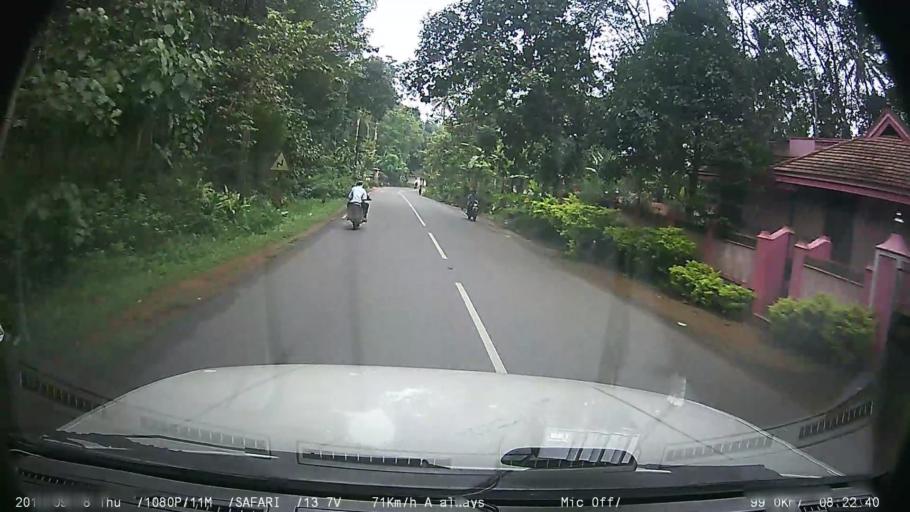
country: IN
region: Kerala
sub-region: Kottayam
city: Palackattumala
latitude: 9.6639
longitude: 76.6094
